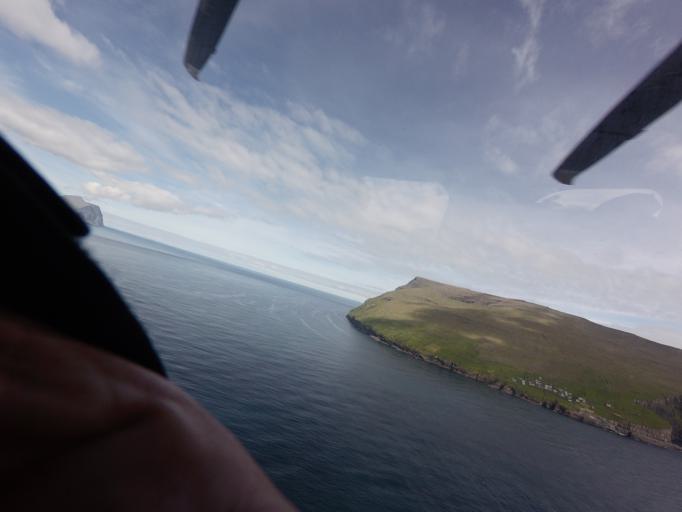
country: FO
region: Nordoyar
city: Klaksvik
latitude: 62.3081
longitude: -6.3274
